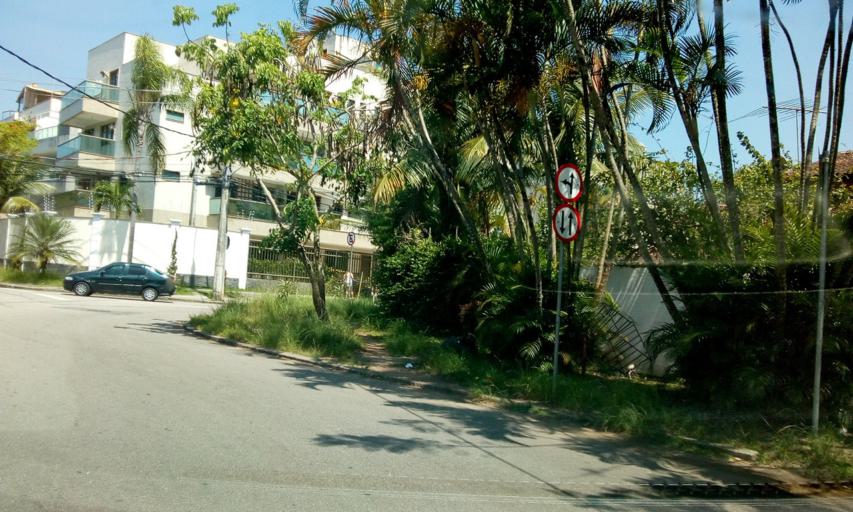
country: BR
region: Rio de Janeiro
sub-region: Nilopolis
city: Nilopolis
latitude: -23.0169
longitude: -43.4695
